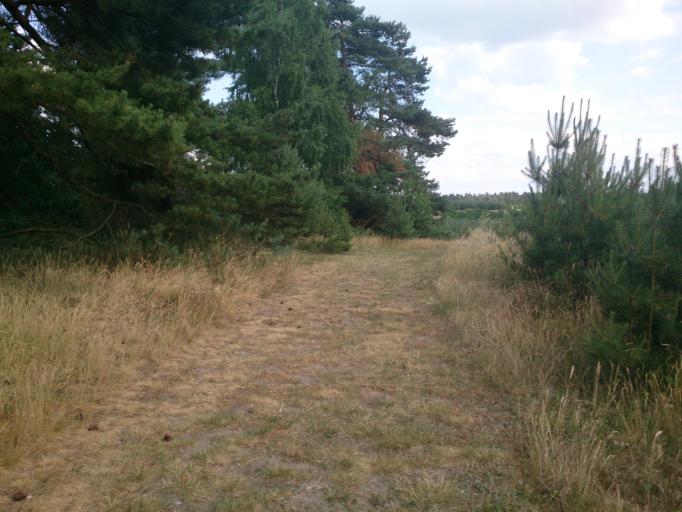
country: DE
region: Mecklenburg-Vorpommern
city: Plau am See
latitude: 53.4275
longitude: 12.3129
